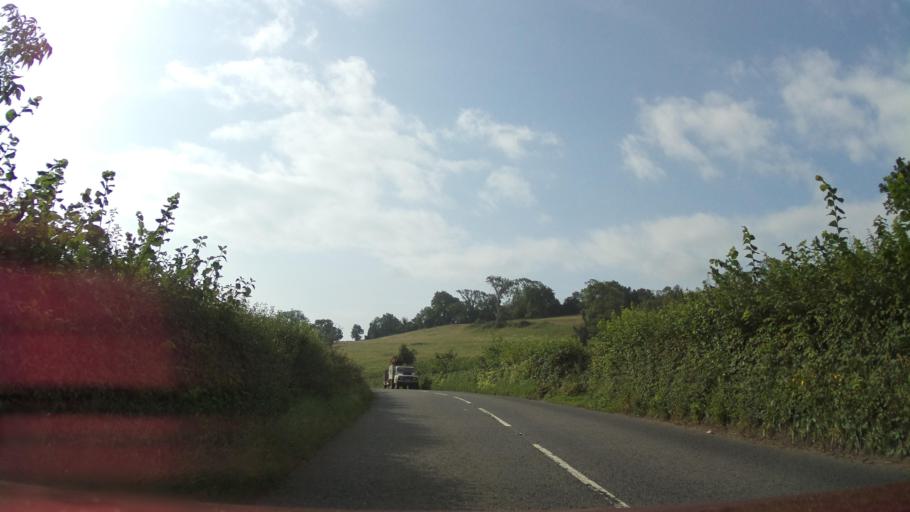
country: GB
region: England
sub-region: North Somerset
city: Winford
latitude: 51.3966
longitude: -2.6699
